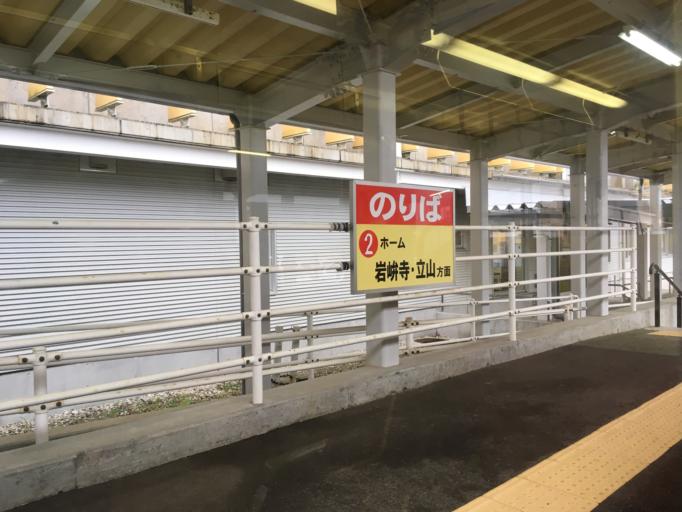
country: JP
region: Toyama
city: Kamiichi
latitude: 36.6655
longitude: 137.3144
